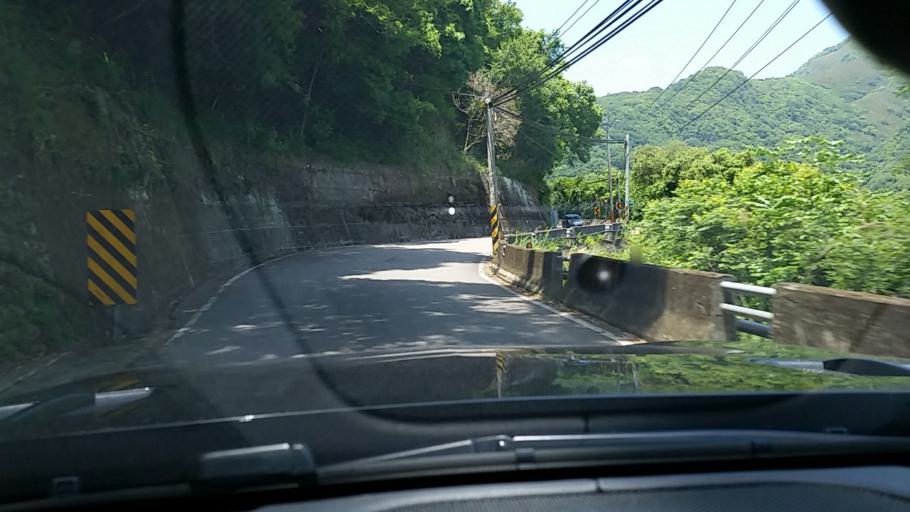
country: TW
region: Taiwan
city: Daxi
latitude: 24.6981
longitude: 121.3753
